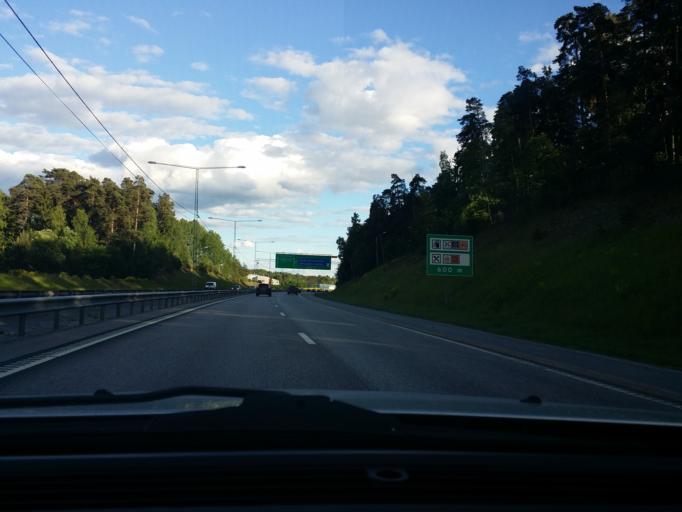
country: SE
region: Stockholm
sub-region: Upplands Vasby Kommun
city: Upplands Vaesby
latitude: 59.5276
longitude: 17.9247
